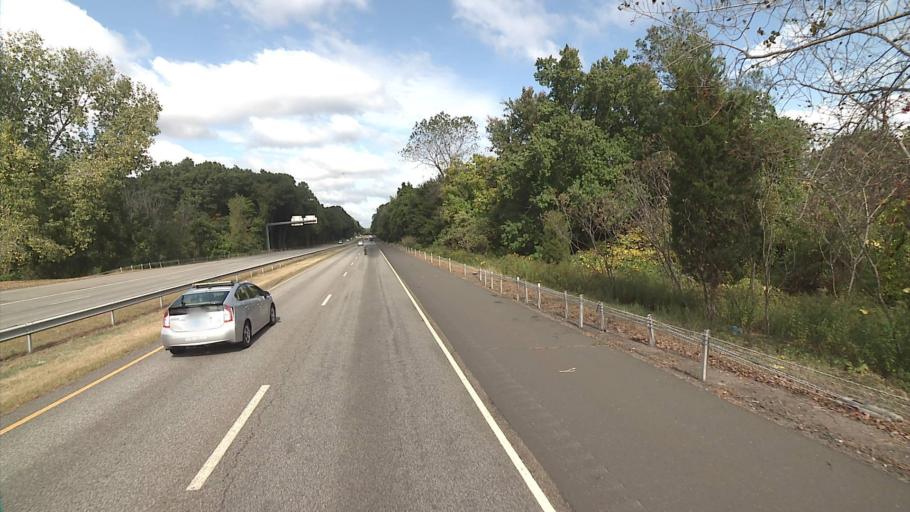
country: US
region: Connecticut
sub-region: New Haven County
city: Wallingford
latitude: 41.4668
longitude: -72.8307
